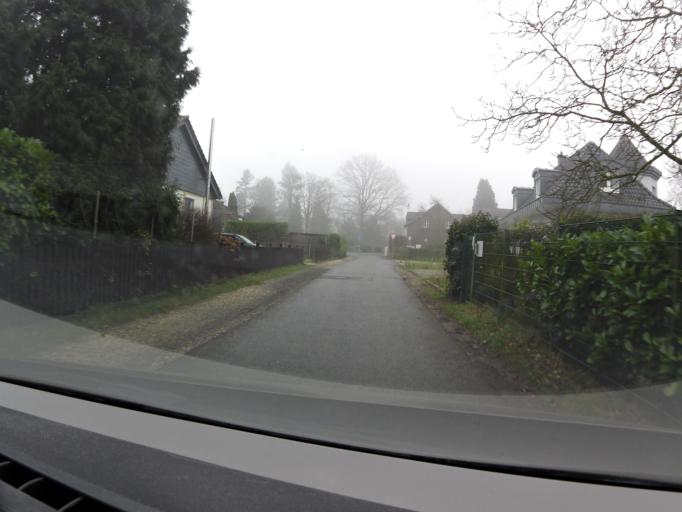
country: DE
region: North Rhine-Westphalia
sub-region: Regierungsbezirk Dusseldorf
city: Nettetal
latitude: 51.3431
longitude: 6.2609
